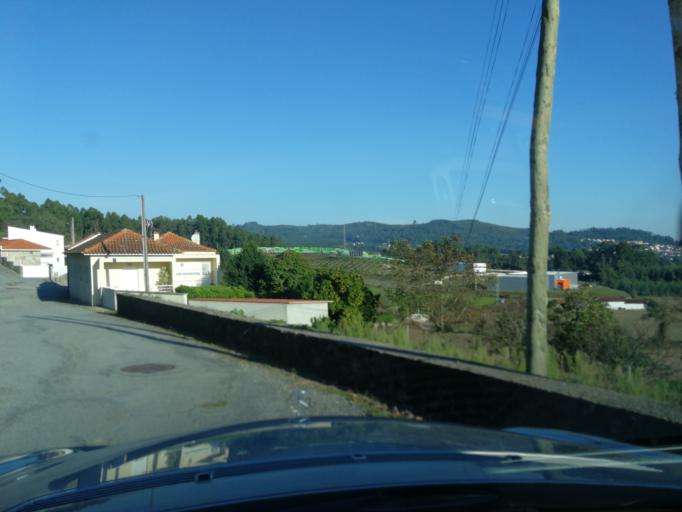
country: PT
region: Braga
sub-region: Vila Nova de Famalicao
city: Vila Nova de Famalicao
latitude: 41.4323
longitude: -8.5035
